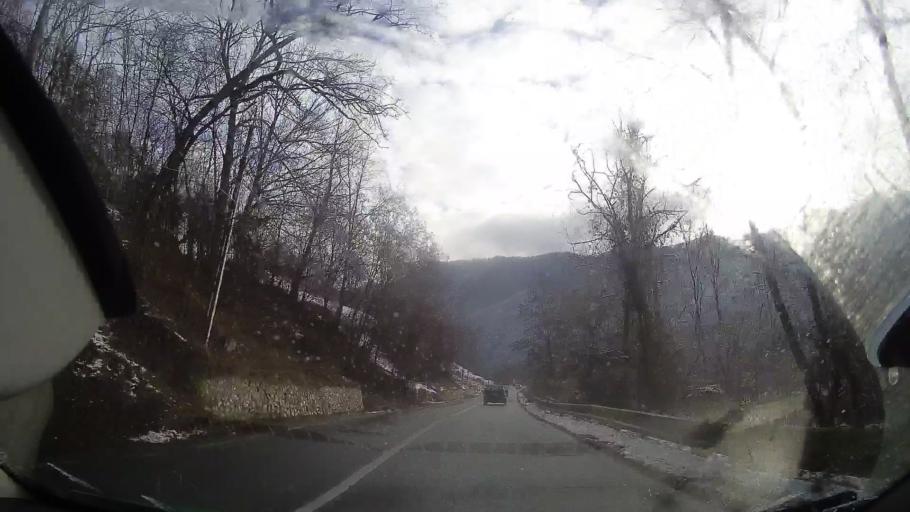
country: RO
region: Alba
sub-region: Oras Baia de Aries
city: Baia de Aries
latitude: 46.4011
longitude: 23.3086
